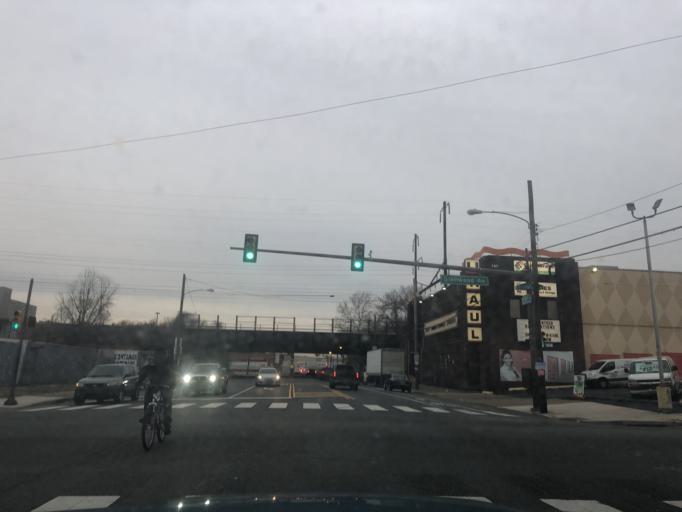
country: US
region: Pennsylvania
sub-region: Philadelphia County
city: Philadelphia
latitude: 40.0006
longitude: -75.1433
